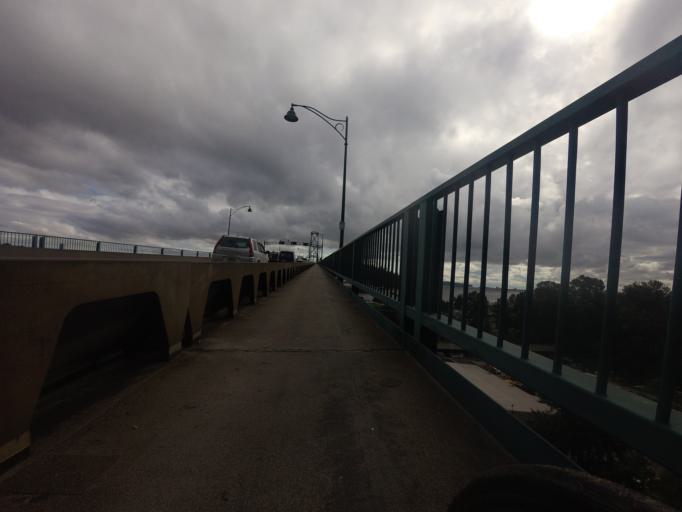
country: CA
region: British Columbia
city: West End
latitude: 49.3213
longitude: -123.1336
